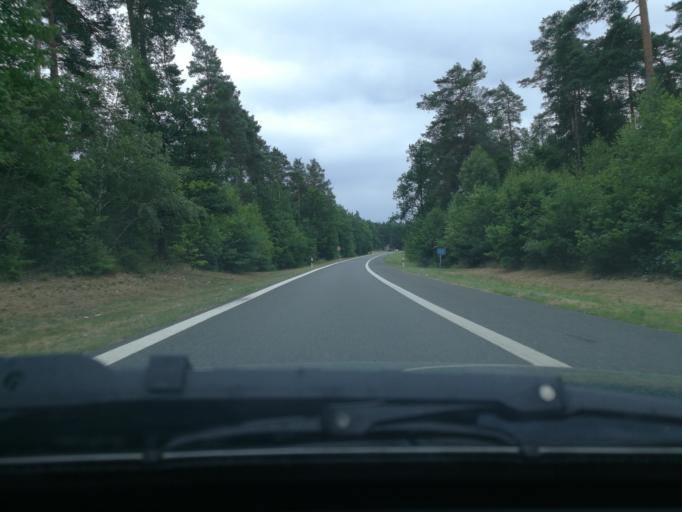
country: DE
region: Bavaria
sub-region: Regierungsbezirk Mittelfranken
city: Heroldsberg
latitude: 49.4998
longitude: 11.1316
